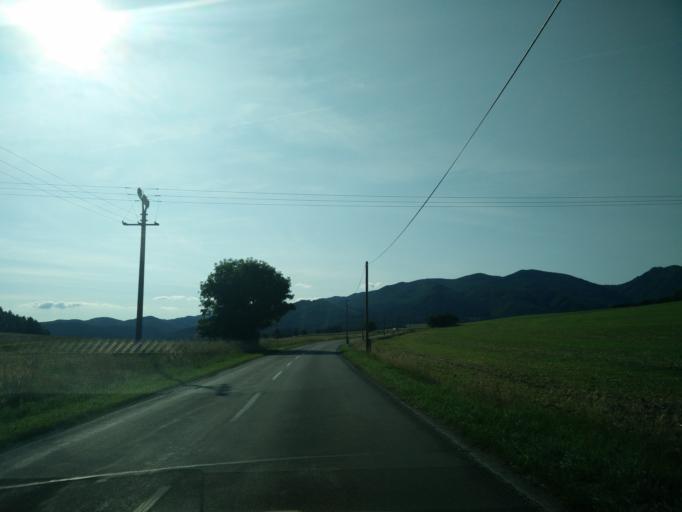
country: SK
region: Zilinsky
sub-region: Okres Martin
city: Martin
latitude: 48.9418
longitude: 18.8226
